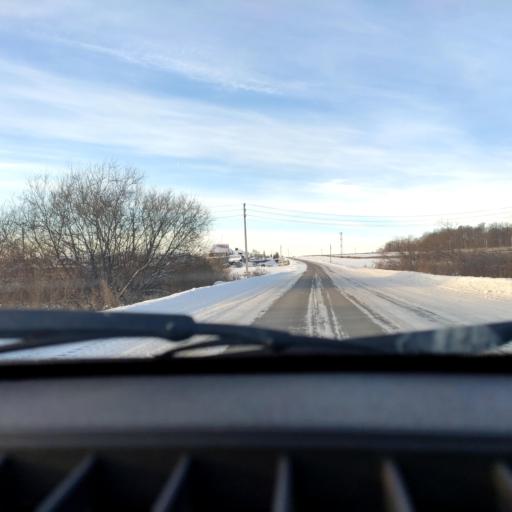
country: RU
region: Bashkortostan
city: Avdon
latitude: 54.6803
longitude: 55.7230
